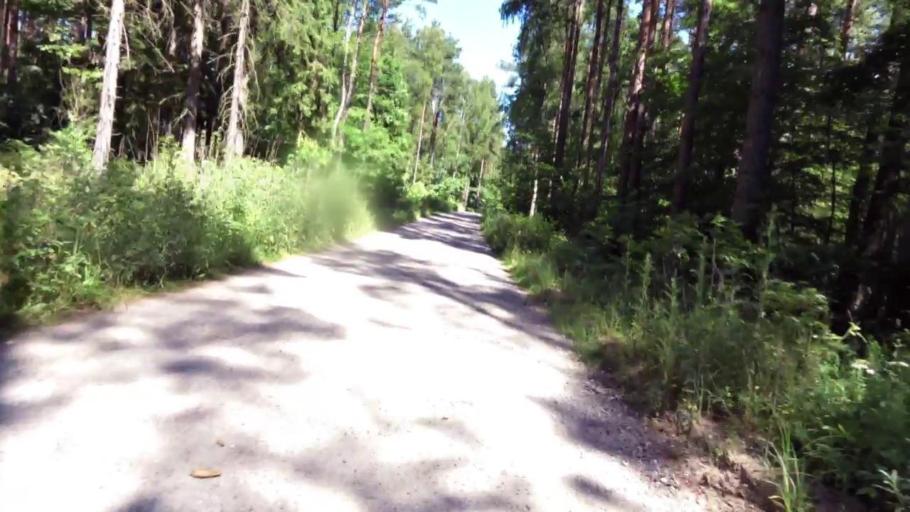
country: PL
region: West Pomeranian Voivodeship
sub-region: Powiat swidwinski
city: Rabino
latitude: 53.8861
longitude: 16.0480
